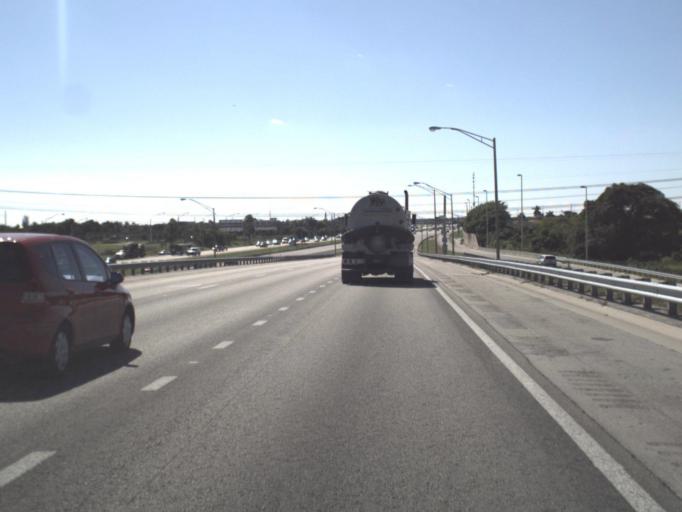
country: US
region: Florida
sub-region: Miami-Dade County
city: Three Lakes
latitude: 25.6475
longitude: -80.3864
